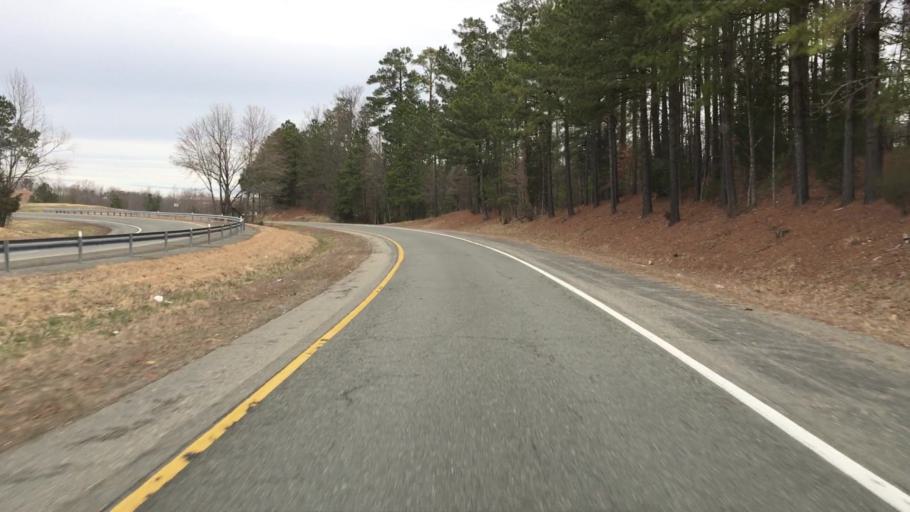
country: US
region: Virginia
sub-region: Henrico County
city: Short Pump
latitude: 37.6353
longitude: -77.5716
